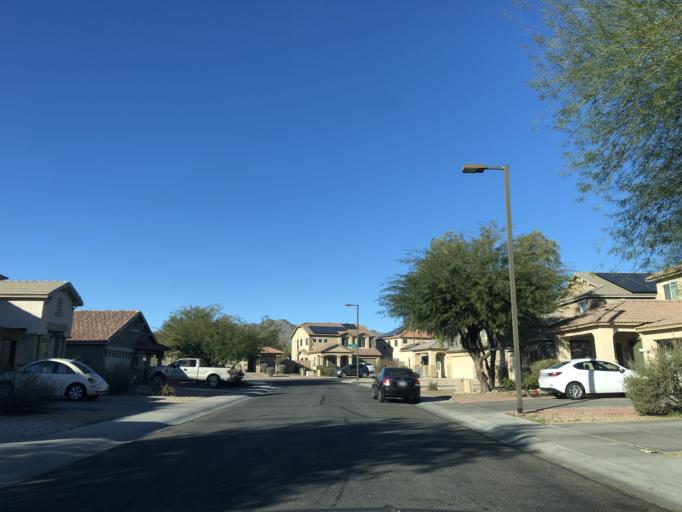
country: US
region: Arizona
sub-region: Maricopa County
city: Buckeye
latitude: 33.4379
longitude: -112.5723
